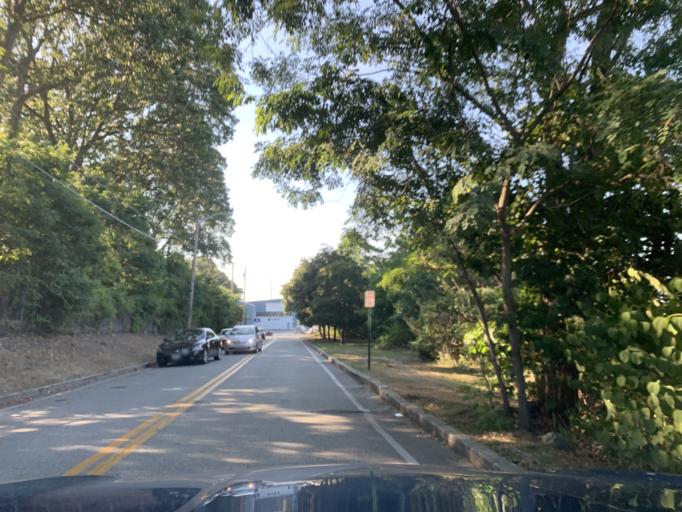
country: US
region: Rhode Island
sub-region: Kent County
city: East Greenwich
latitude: 41.6838
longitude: -71.4500
